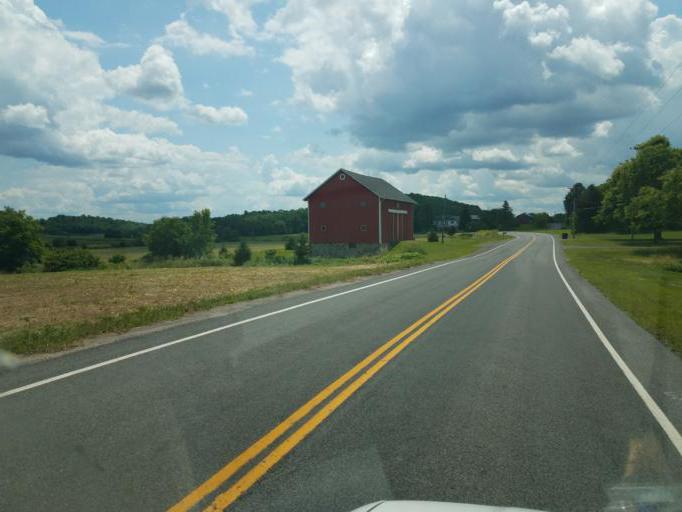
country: US
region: New York
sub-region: Wayne County
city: Clyde
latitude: 43.0631
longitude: -76.8574
